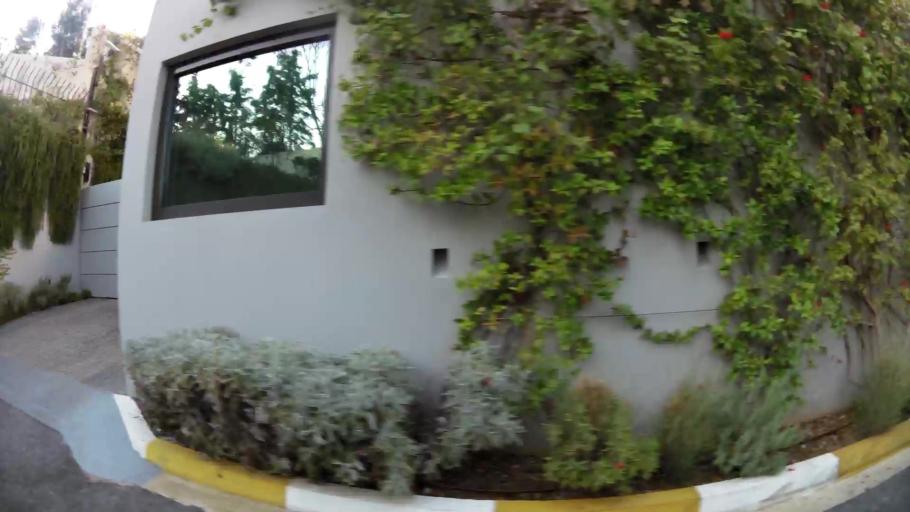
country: GR
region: Attica
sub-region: Nomarchia Anatolikis Attikis
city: Vari
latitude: 37.8239
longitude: 23.7936
